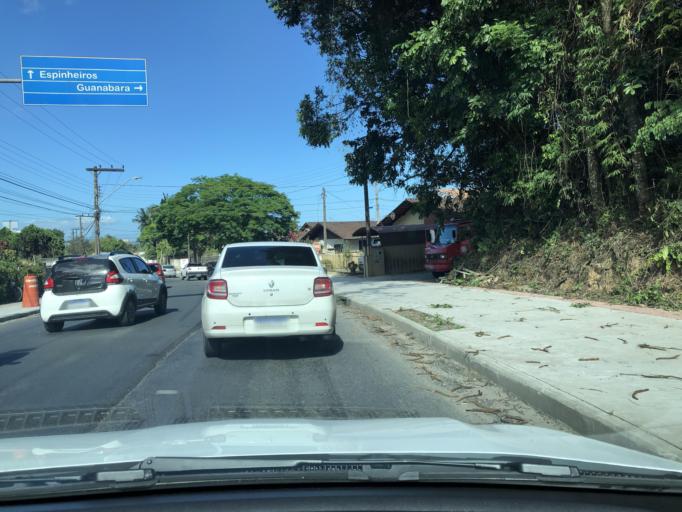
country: BR
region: Santa Catarina
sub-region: Joinville
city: Joinville
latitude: -26.3109
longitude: -48.8309
